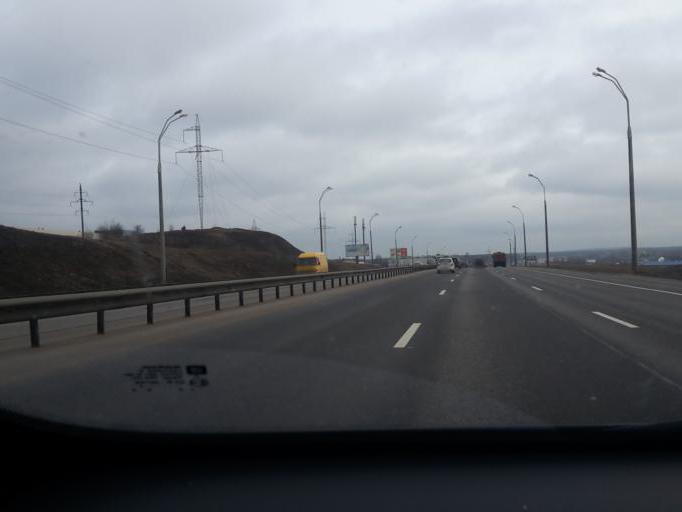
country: BY
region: Minsk
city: Zhdanovichy
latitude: 53.9334
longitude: 27.4240
